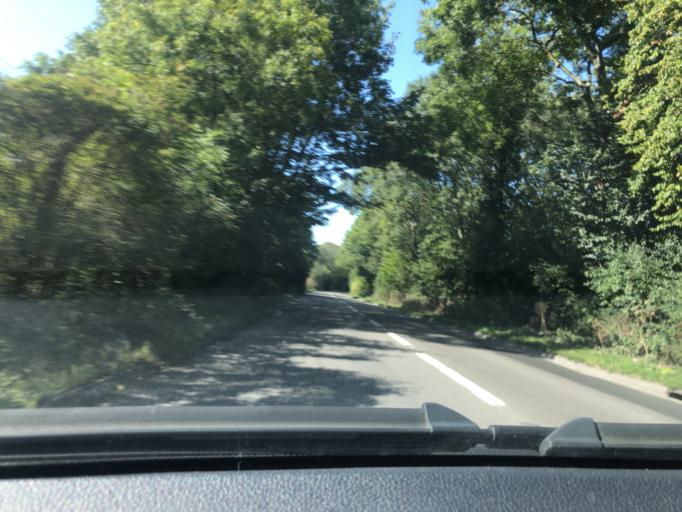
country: GB
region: England
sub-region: Somerset
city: Puriton
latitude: 51.1559
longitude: -2.9593
